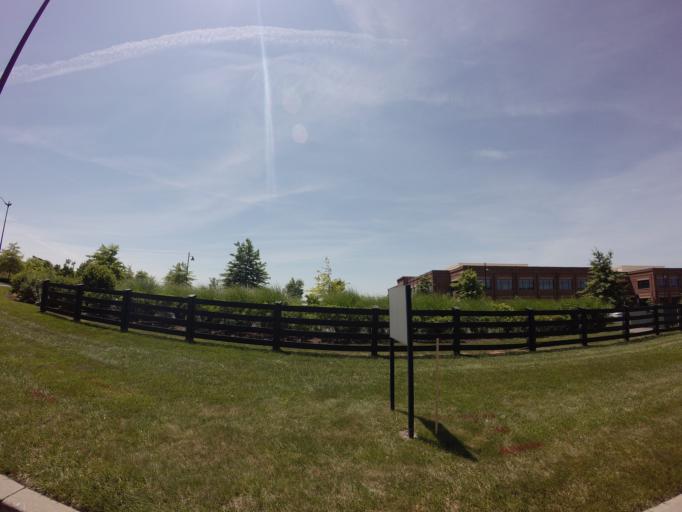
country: US
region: Maryland
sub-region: Frederick County
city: Urbana
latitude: 39.3244
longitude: -77.3501
